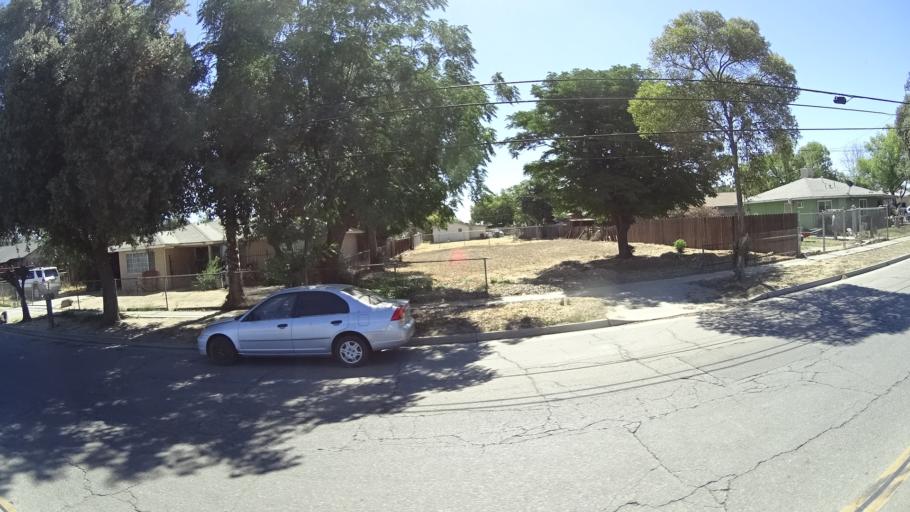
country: US
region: California
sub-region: Fresno County
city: Easton
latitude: 36.6950
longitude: -119.7998
